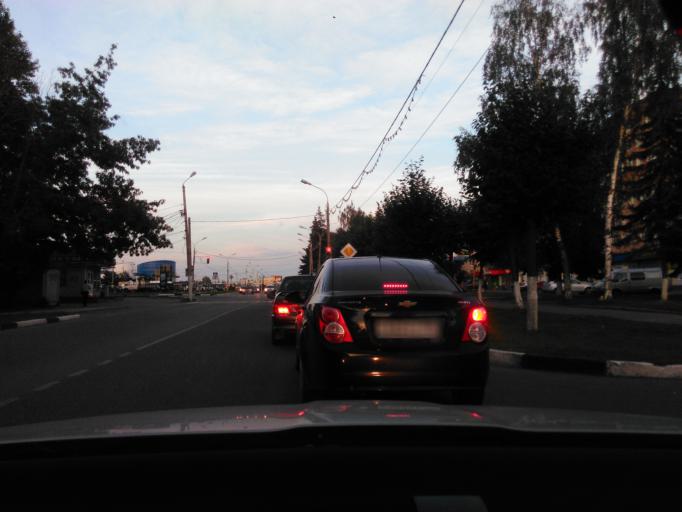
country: RU
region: Moskovskaya
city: Klin
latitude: 56.3195
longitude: 36.7264
